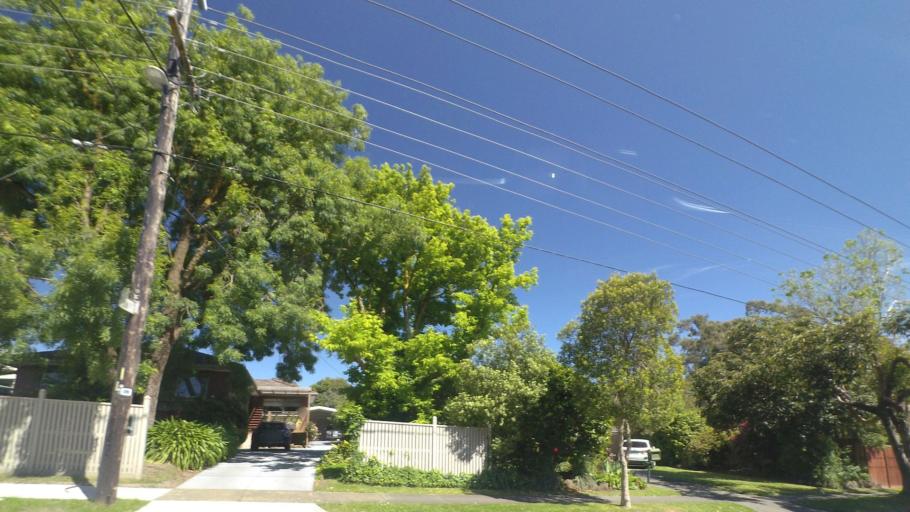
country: AU
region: Victoria
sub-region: Maroondah
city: Heathmont
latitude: -37.8253
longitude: 145.2592
